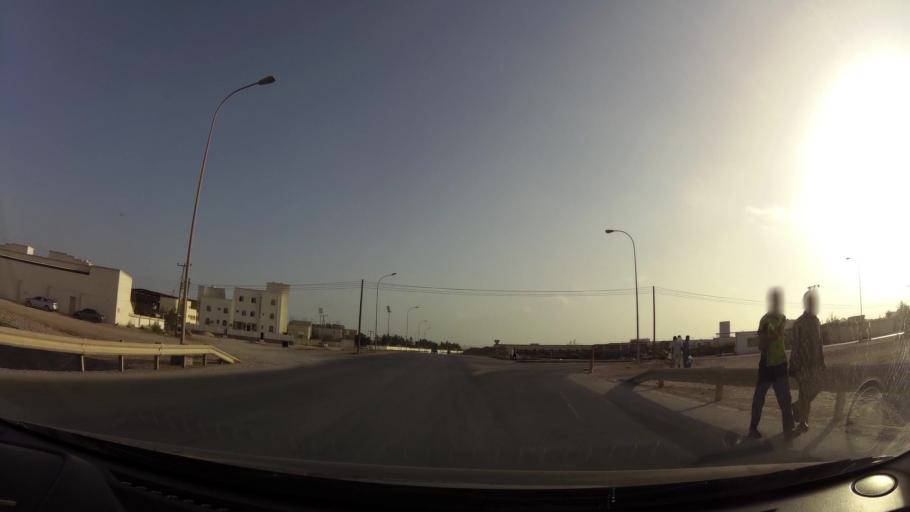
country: OM
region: Zufar
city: Salalah
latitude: 16.9978
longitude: 54.0270
